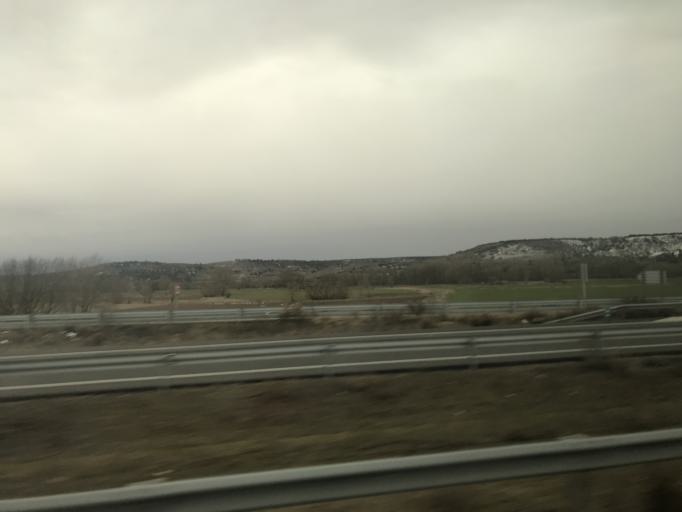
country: ES
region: Castille and Leon
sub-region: Provincia de Burgos
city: Celada del Camino
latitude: 42.2603
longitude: -3.9431
